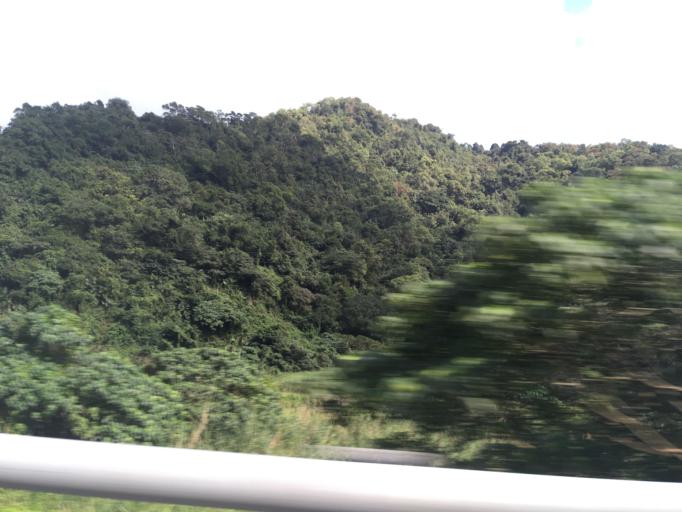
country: TW
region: Taiwan
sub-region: Yilan
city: Yilan
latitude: 24.7504
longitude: 121.6653
